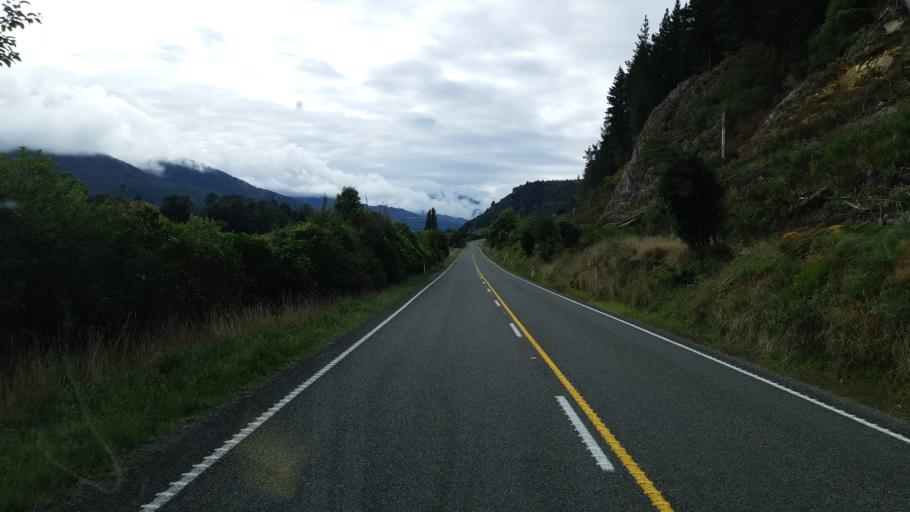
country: NZ
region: West Coast
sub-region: Buller District
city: Westport
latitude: -41.7790
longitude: 172.2491
